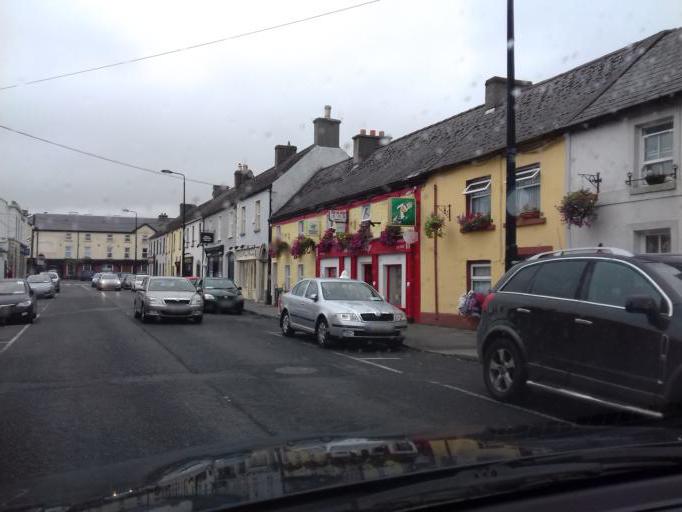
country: IE
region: Leinster
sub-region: County Carlow
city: Bagenalstown
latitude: 52.7013
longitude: -6.9572
